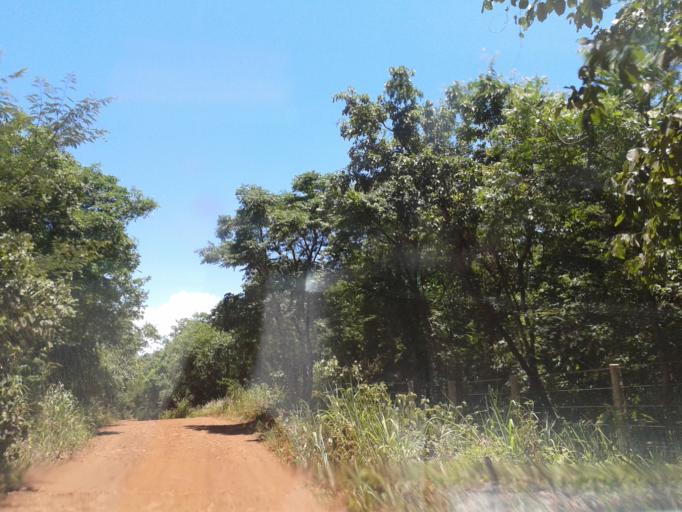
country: BR
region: Minas Gerais
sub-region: Centralina
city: Centralina
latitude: -18.6865
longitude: -49.2226
